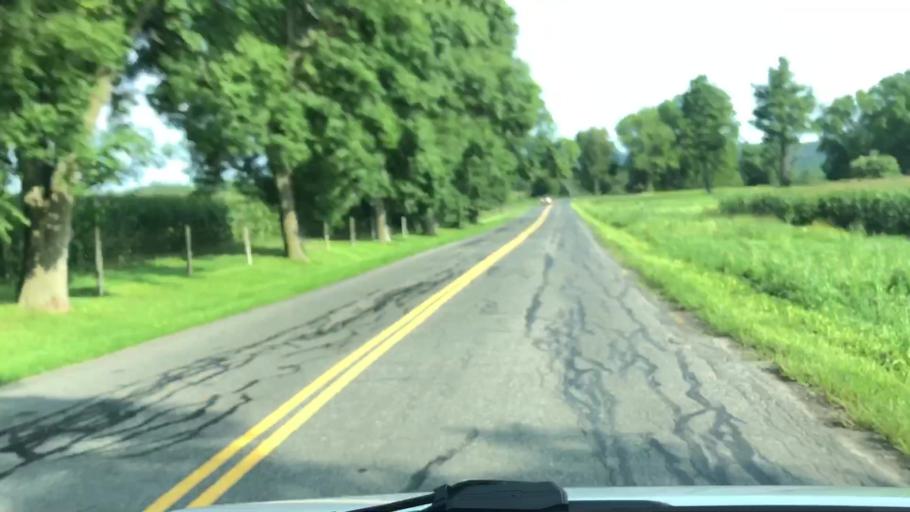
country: US
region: Massachusetts
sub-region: Berkshire County
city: Lee
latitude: 42.3175
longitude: -73.2729
